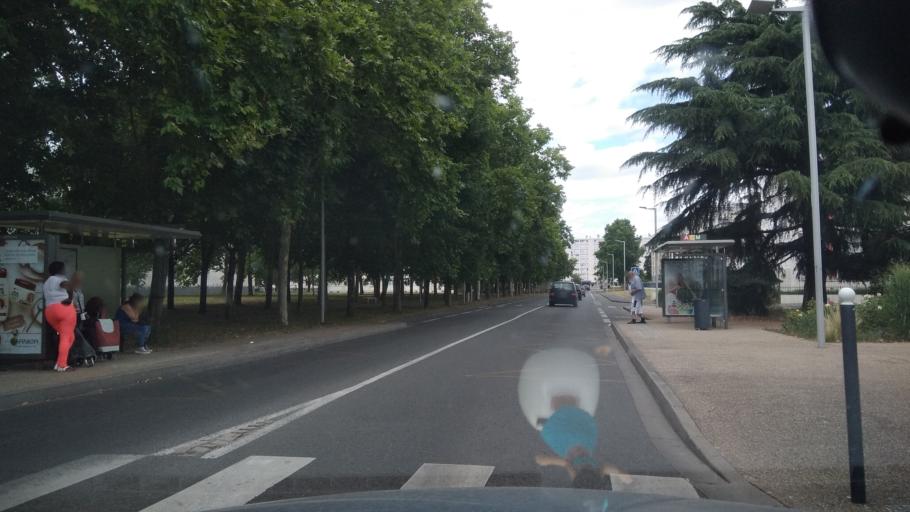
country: FR
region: Poitou-Charentes
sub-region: Departement de la Vienne
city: Chatellerault
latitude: 46.8024
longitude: 0.5412
